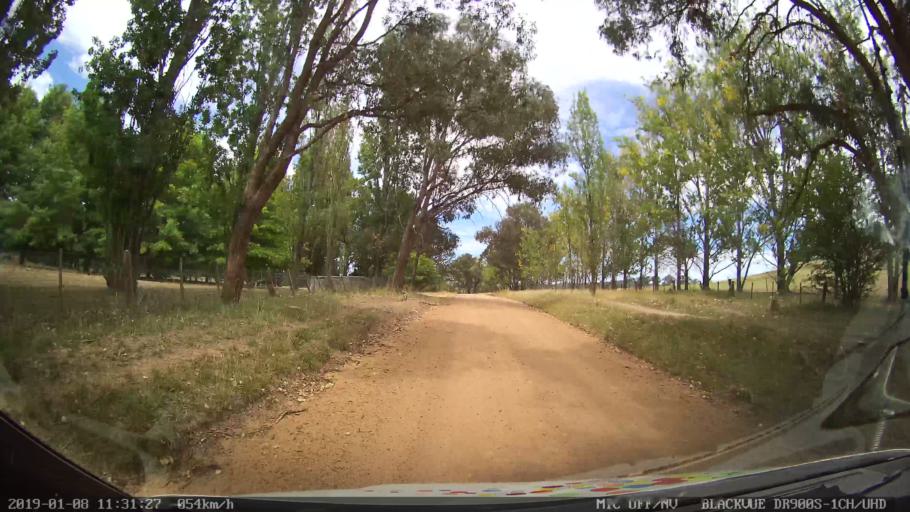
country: AU
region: New South Wales
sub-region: Guyra
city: Guyra
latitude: -30.3124
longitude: 151.5370
